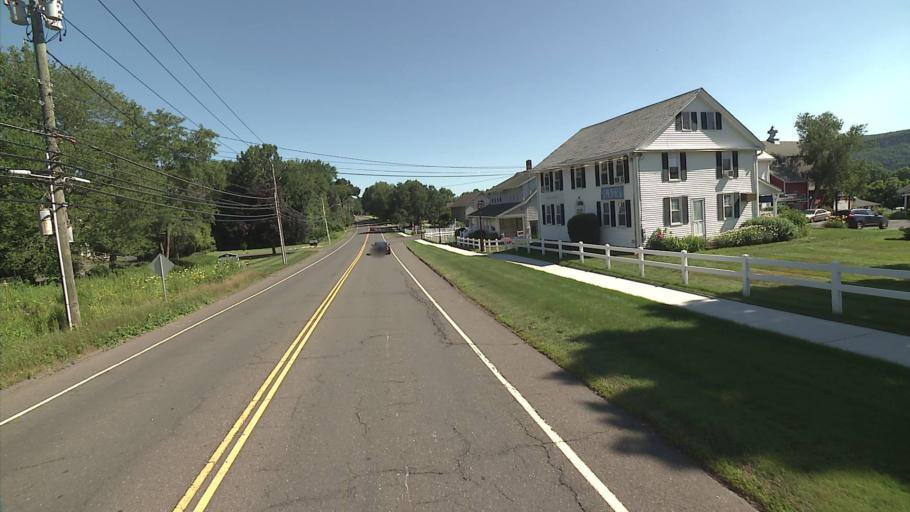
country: US
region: Connecticut
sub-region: Hartford County
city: Weatogue
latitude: 41.8188
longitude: -72.8297
